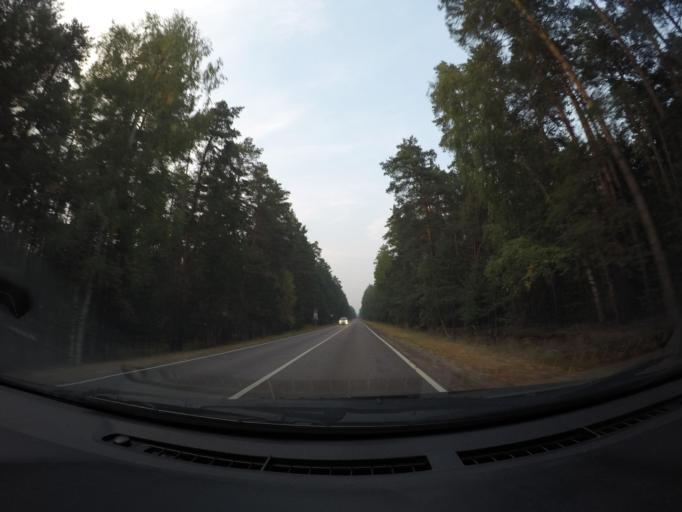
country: RU
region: Moskovskaya
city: Imeni Tsyurupy
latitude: 55.5097
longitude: 38.7178
